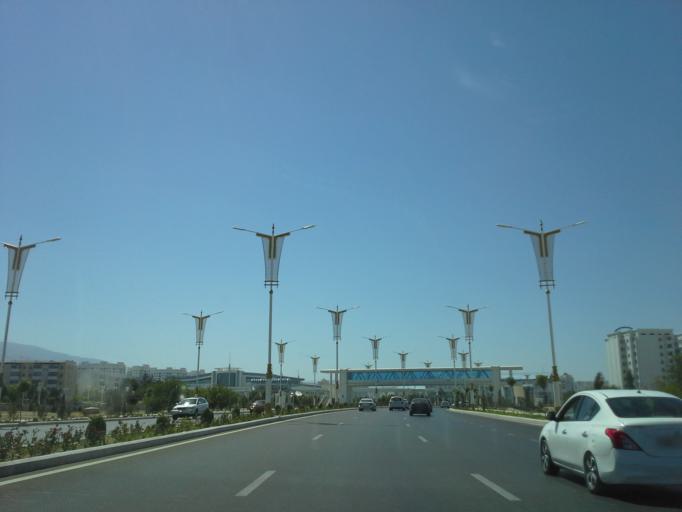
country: TM
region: Ahal
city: Ashgabat
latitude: 37.9105
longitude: 58.3869
